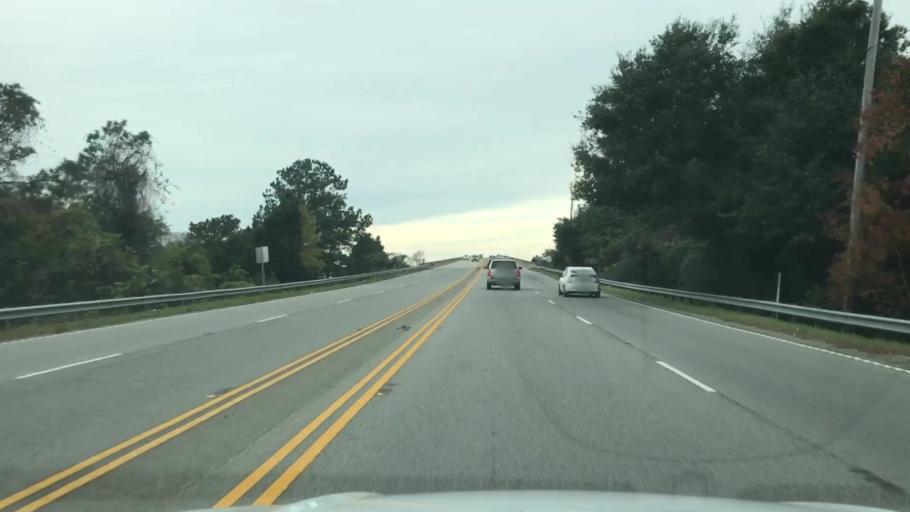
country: US
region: South Carolina
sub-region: Georgetown County
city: Georgetown
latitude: 33.3652
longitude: -79.2474
